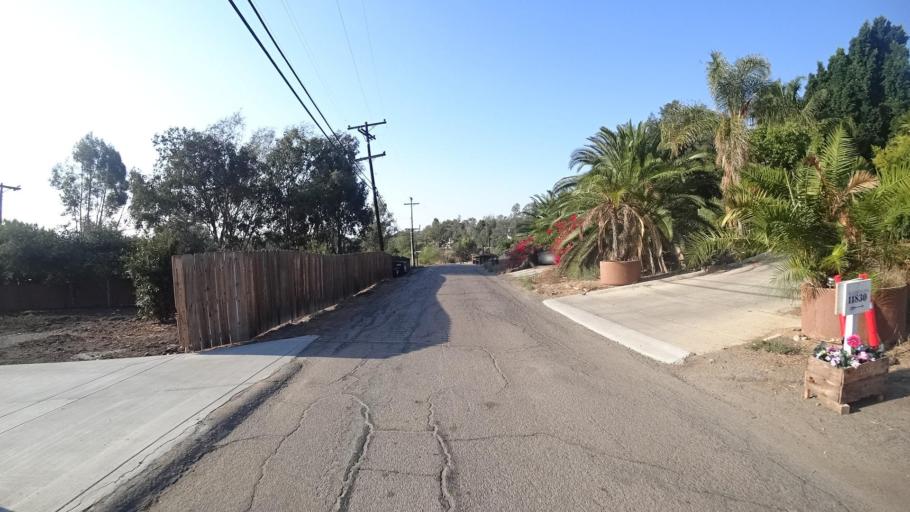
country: US
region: California
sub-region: San Diego County
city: Eucalyptus Hills
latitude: 32.8932
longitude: -116.9482
